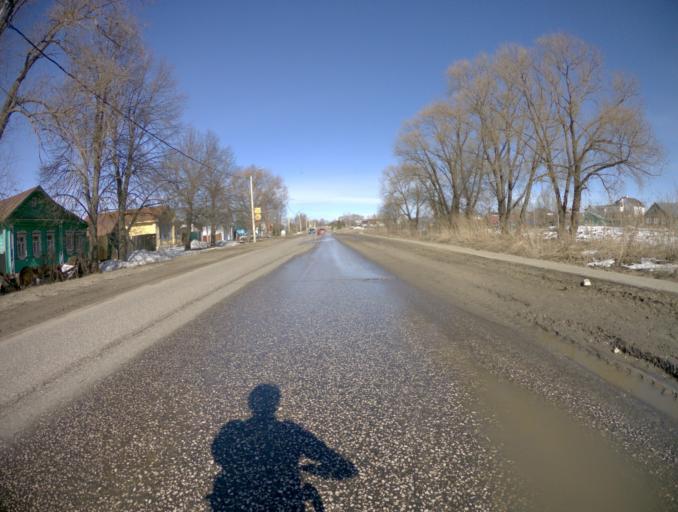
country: RU
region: Vladimir
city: Suzdal'
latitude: 56.4351
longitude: 40.4292
